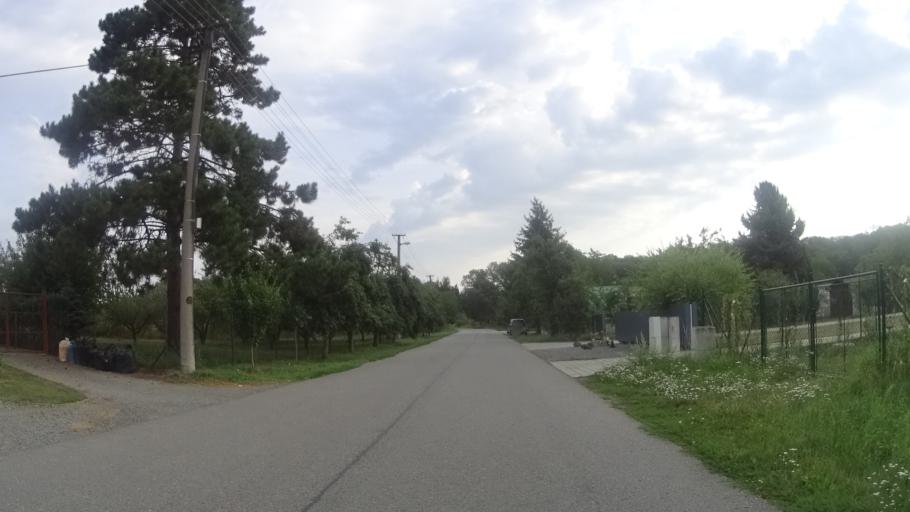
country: CZ
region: Zlin
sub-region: Okres Kromeriz
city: Kromeriz
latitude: 49.3191
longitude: 17.3891
